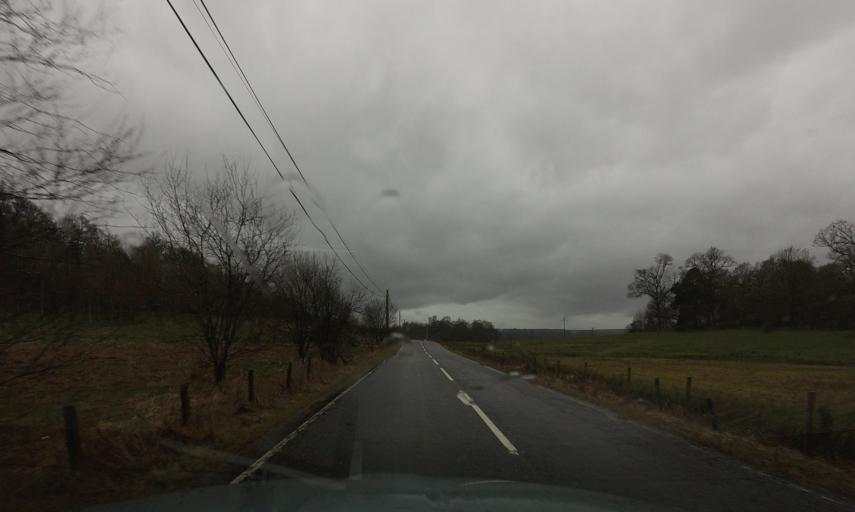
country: GB
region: Scotland
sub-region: Stirling
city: Balfron
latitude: 56.1442
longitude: -4.3607
